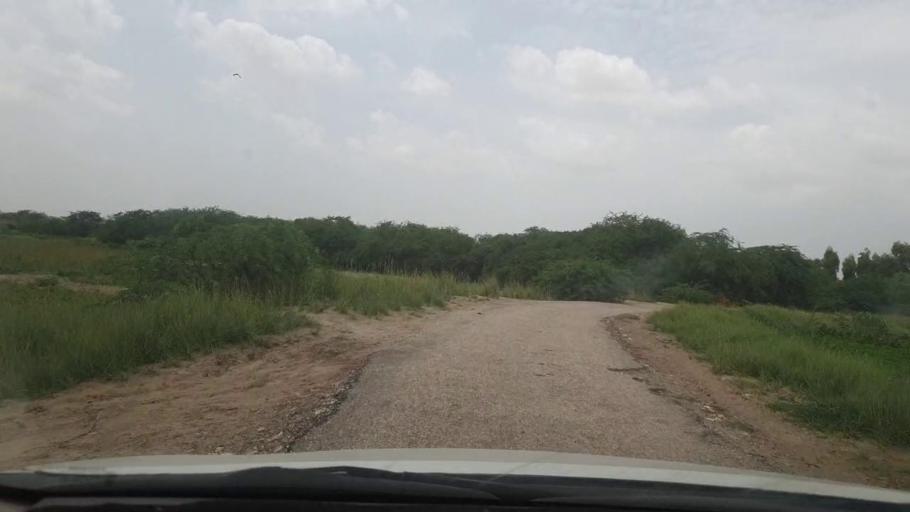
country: PK
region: Sindh
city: Khairpur
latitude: 27.3715
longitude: 68.9859
